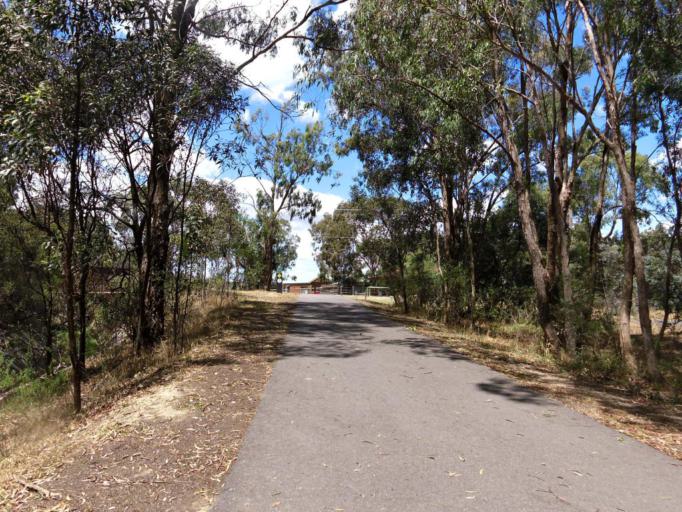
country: AU
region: Victoria
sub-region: Nillumbik
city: Research
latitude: -37.6943
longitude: 145.1686
